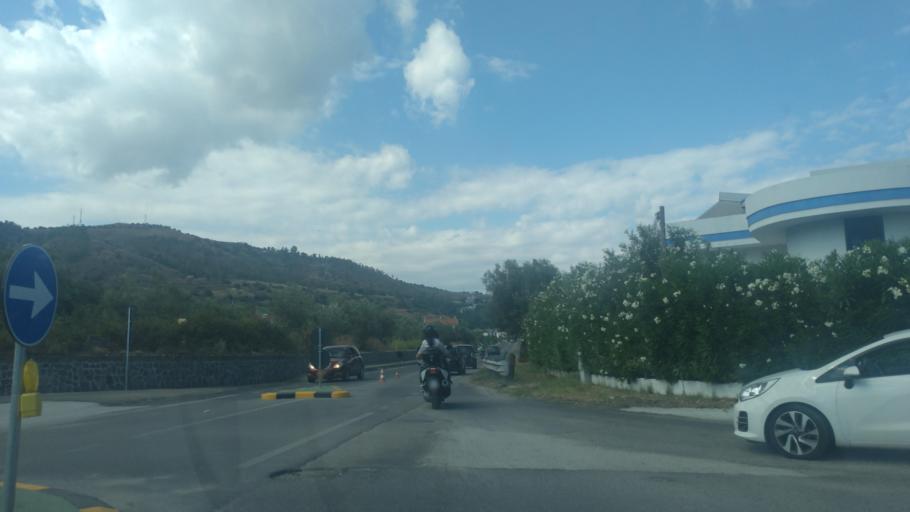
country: IT
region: Calabria
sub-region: Provincia di Catanzaro
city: Montepaone Lido
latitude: 38.7365
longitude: 16.5465
